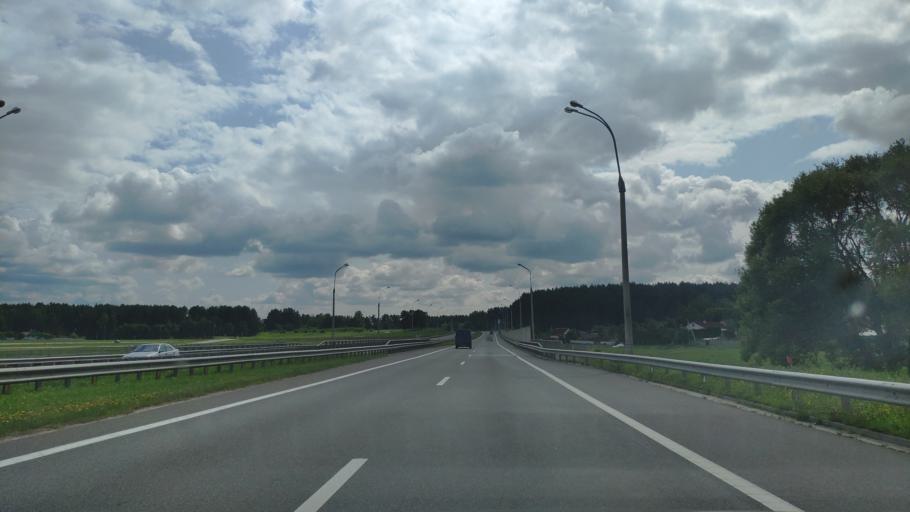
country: BY
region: Minsk
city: Zaslawye
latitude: 53.9979
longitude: 27.3067
